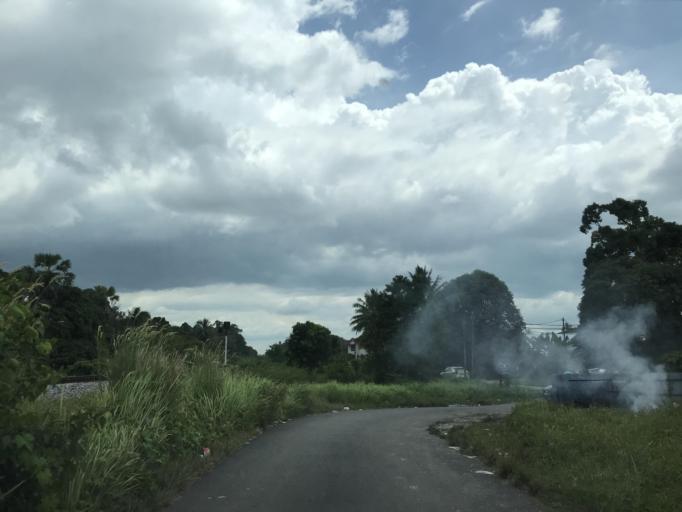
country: MY
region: Kelantan
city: Kota Bharu
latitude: 6.1123
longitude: 102.1935
